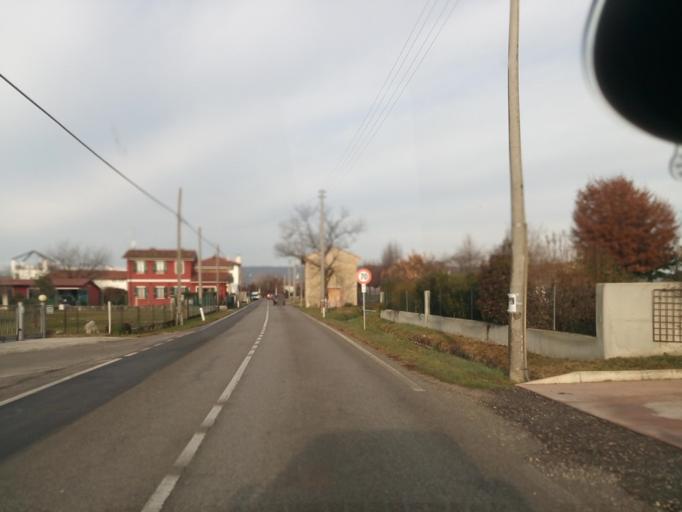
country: IT
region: Veneto
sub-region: Provincia di Treviso
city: Selva del Montello
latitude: 45.7687
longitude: 12.1491
